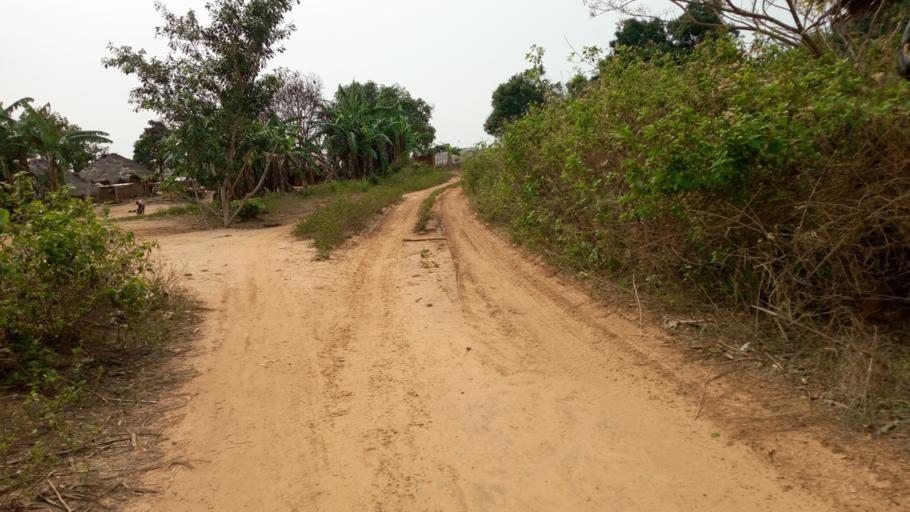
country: CD
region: Bandundu
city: Bandundu
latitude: -3.4515
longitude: 17.7679
